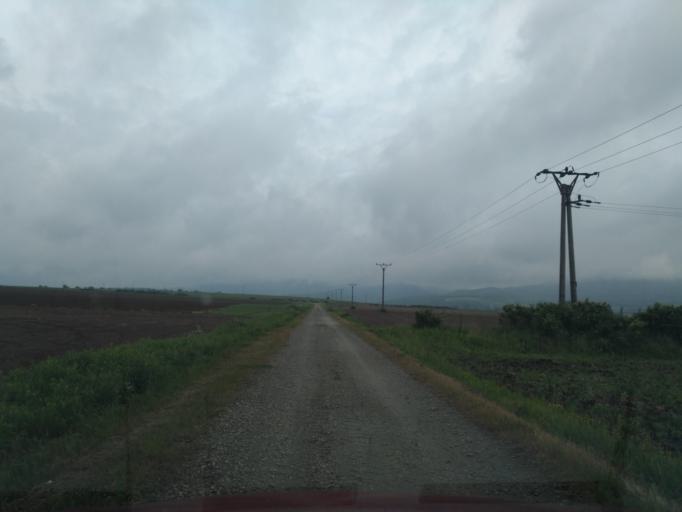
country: SK
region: Kosicky
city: Secovce
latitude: 48.7618
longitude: 21.4713
